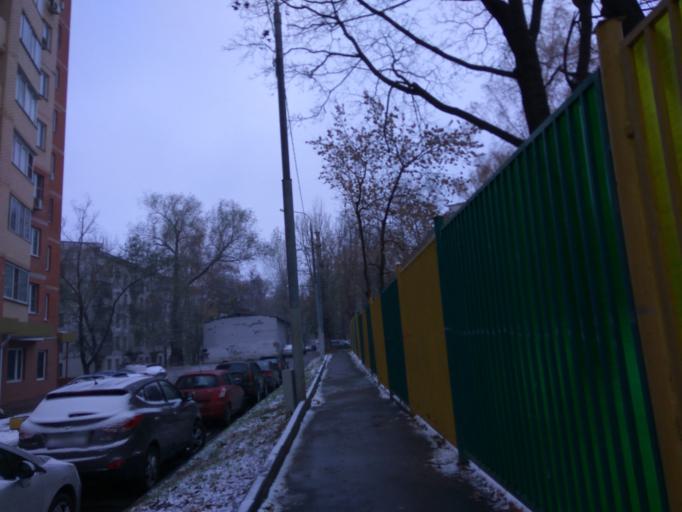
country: RU
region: Moscow
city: Orekhovo-Borisovo Severnoye
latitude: 55.6323
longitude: 37.6753
